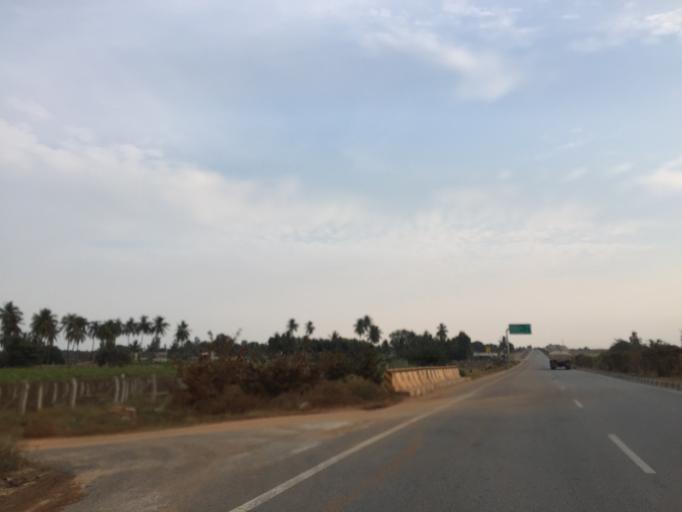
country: IN
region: Karnataka
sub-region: Chikkaballapur
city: Chik Ballapur
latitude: 13.4198
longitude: 77.7443
